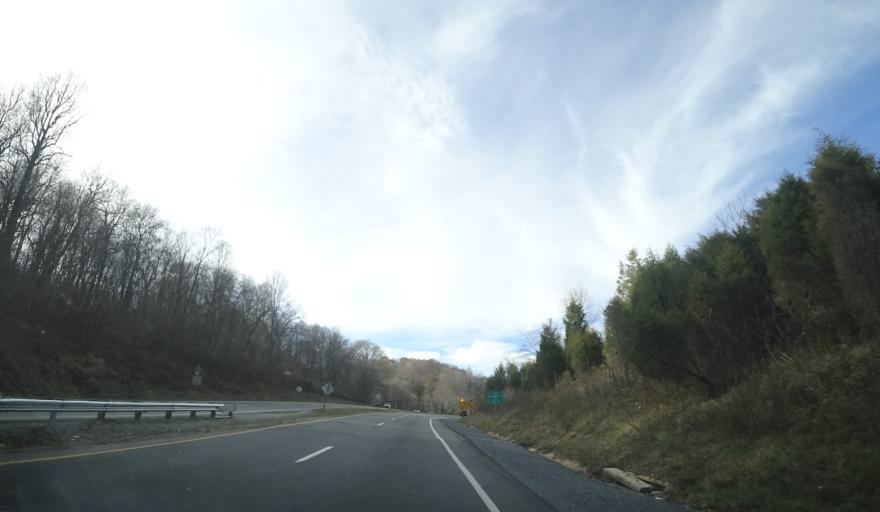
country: US
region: Virginia
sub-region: Rockingham County
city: Elkton
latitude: 38.3569
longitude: -78.5453
